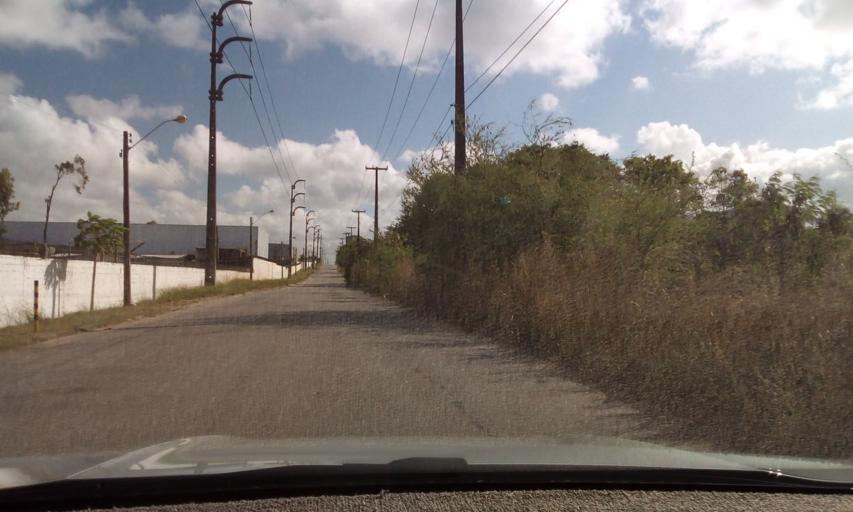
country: BR
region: Paraiba
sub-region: Bayeux
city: Bayeux
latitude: -7.1720
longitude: -34.9065
